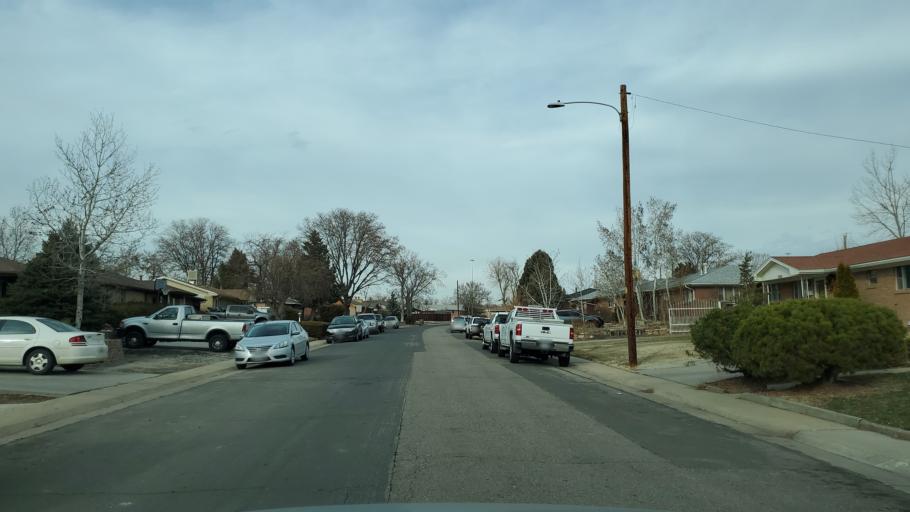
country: US
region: Colorado
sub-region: Adams County
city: Twin Lakes
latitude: 39.8324
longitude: -105.0197
